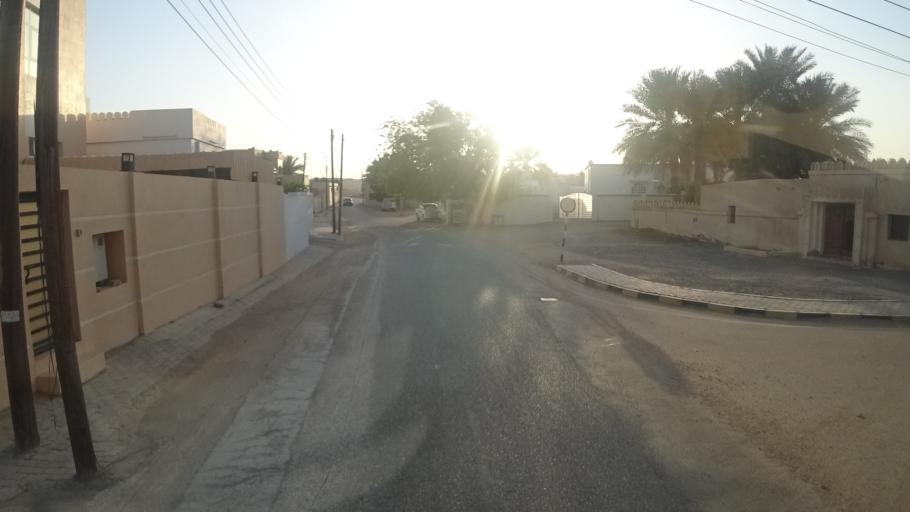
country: OM
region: Ash Sharqiyah
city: Badiyah
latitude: 22.4999
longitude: 58.7423
